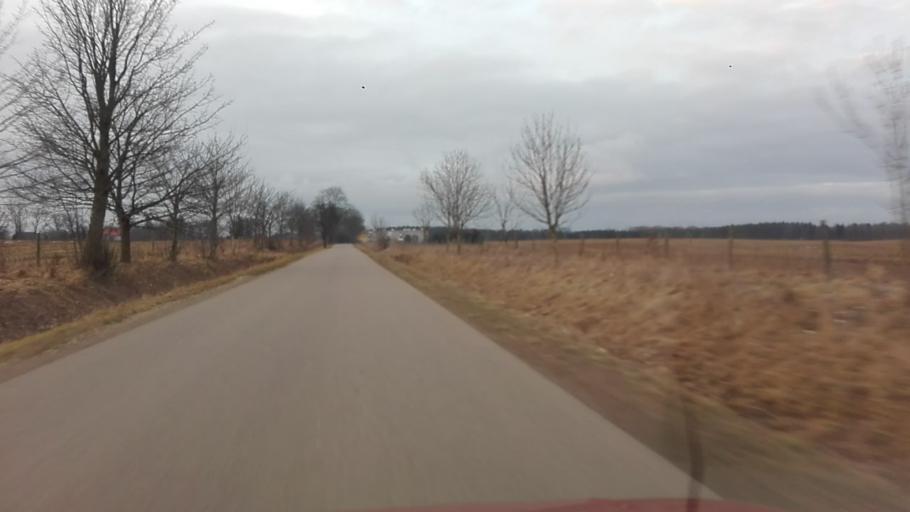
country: PL
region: West Pomeranian Voivodeship
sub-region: Powiat swidwinski
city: Rabino
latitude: 53.8179
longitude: 15.9260
